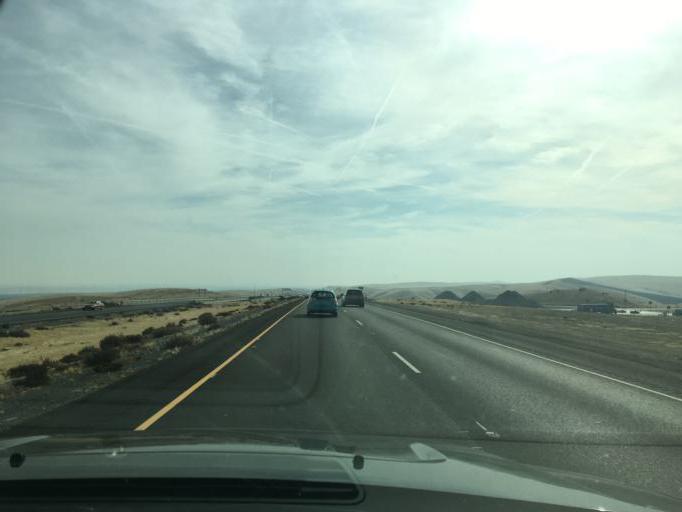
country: US
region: California
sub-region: Kings County
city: Kettleman City
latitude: 35.9829
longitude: -119.9619
